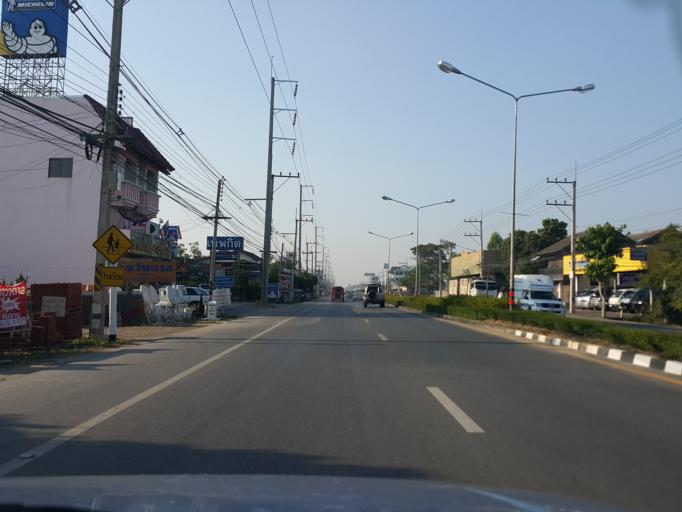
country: TH
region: Chiang Mai
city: San Pa Tong
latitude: 18.6488
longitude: 98.9036
